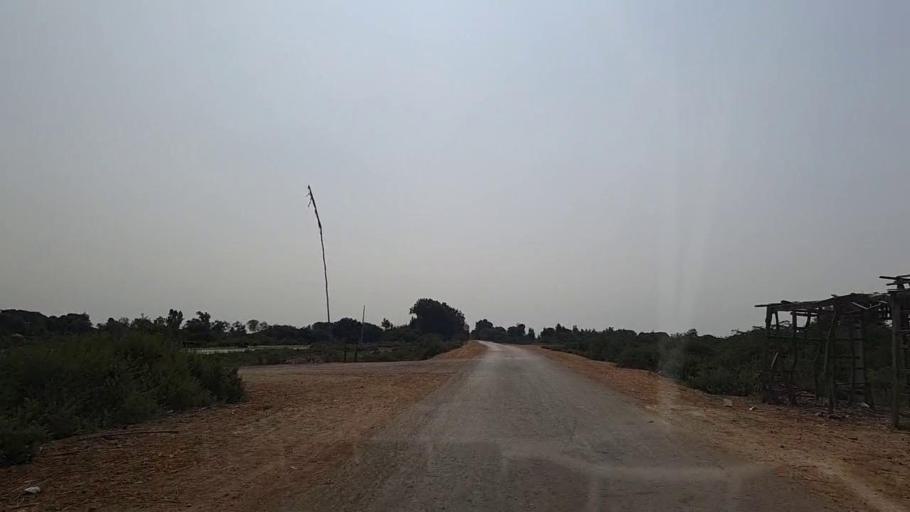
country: PK
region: Sindh
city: Chuhar Jamali
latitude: 24.2486
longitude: 67.9051
